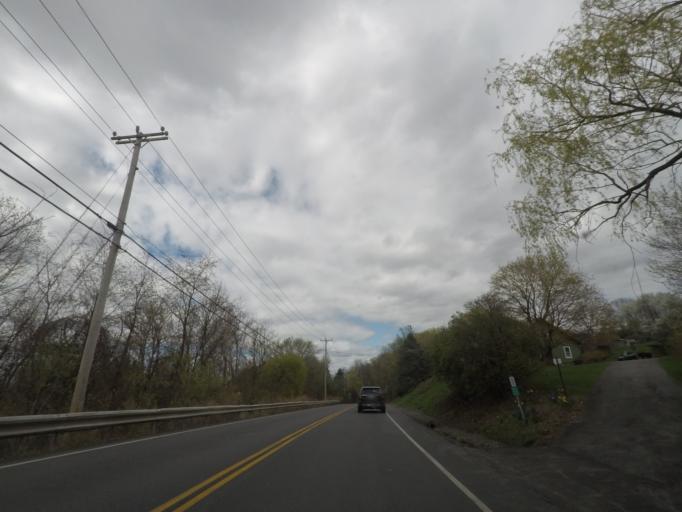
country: US
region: New York
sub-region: Columbia County
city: Chatham
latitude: 42.3635
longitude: -73.6164
